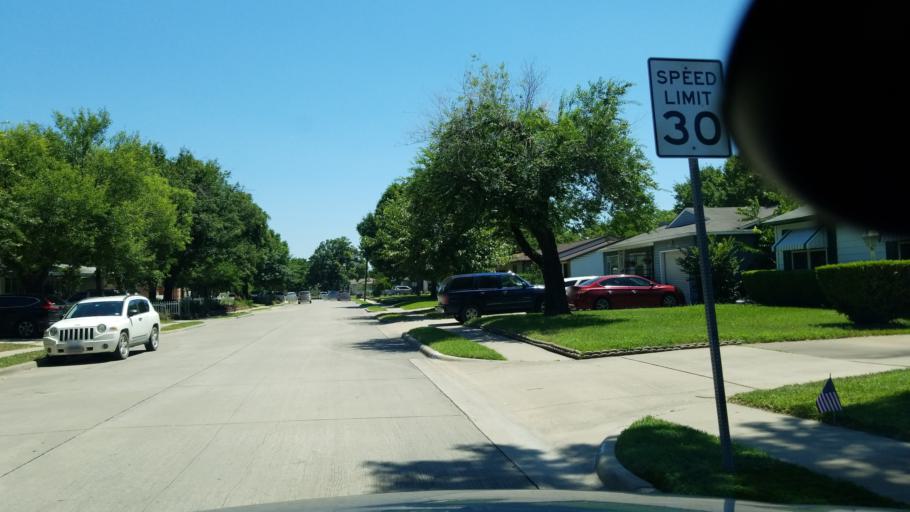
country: US
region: Texas
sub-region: Dallas County
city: Irving
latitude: 32.8345
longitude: -96.9334
